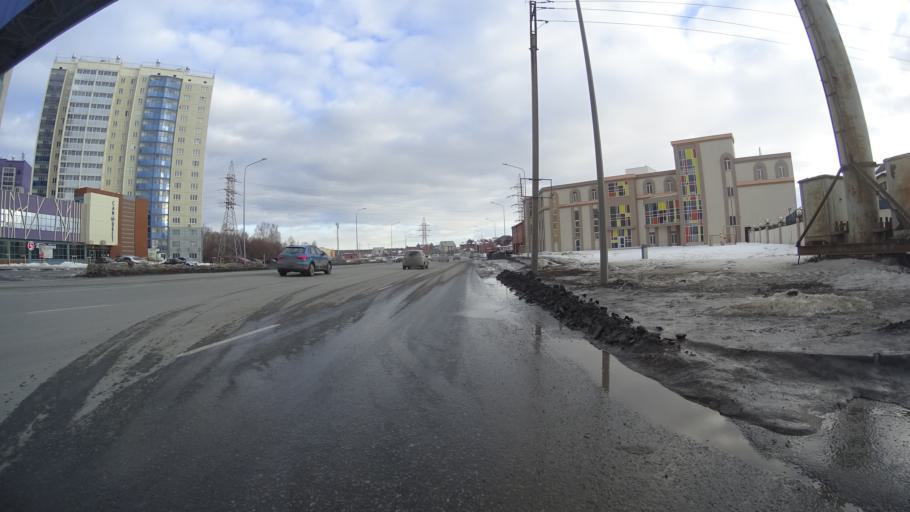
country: RU
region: Chelyabinsk
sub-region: Gorod Chelyabinsk
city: Chelyabinsk
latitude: 55.1583
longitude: 61.3048
